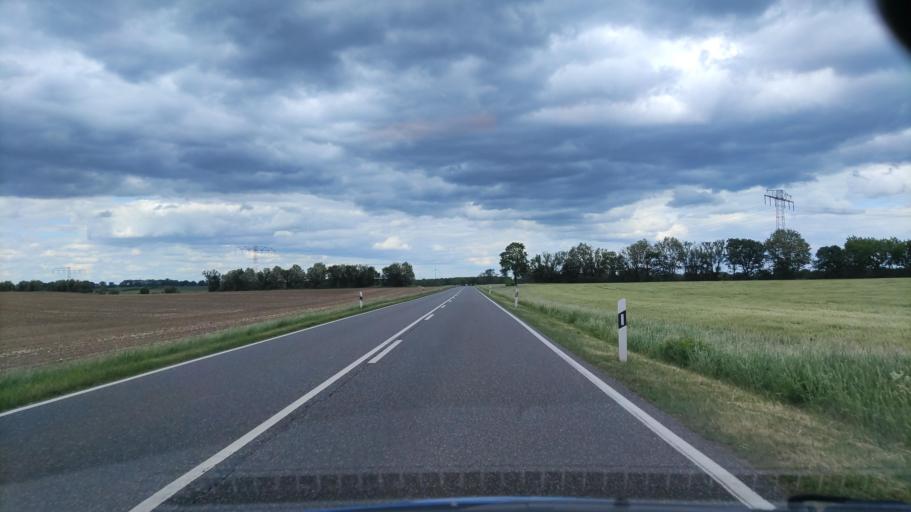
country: DE
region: Mecklenburg-Vorpommern
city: Neuburg
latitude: 53.4441
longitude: 11.9134
